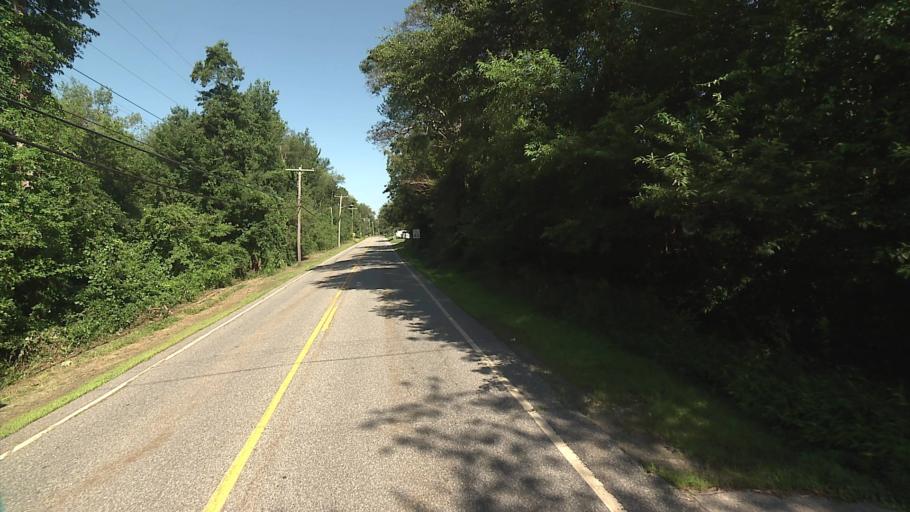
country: US
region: Connecticut
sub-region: New London County
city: Montville Center
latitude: 41.4890
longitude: -72.1711
